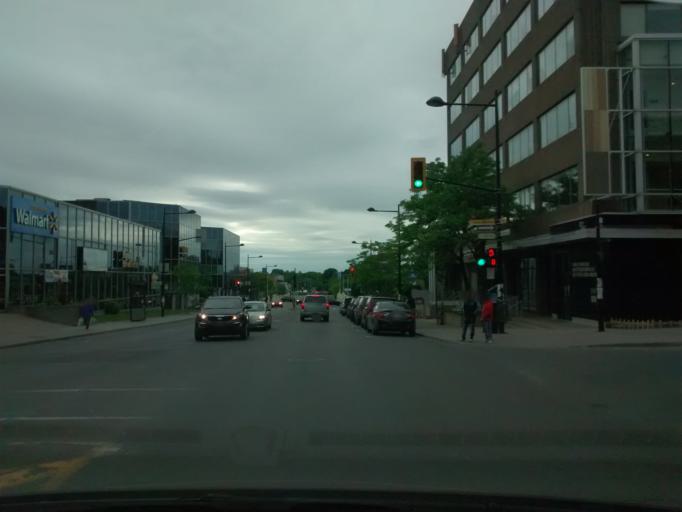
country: CA
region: Quebec
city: Mont-Royal
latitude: 45.5029
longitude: -73.6367
